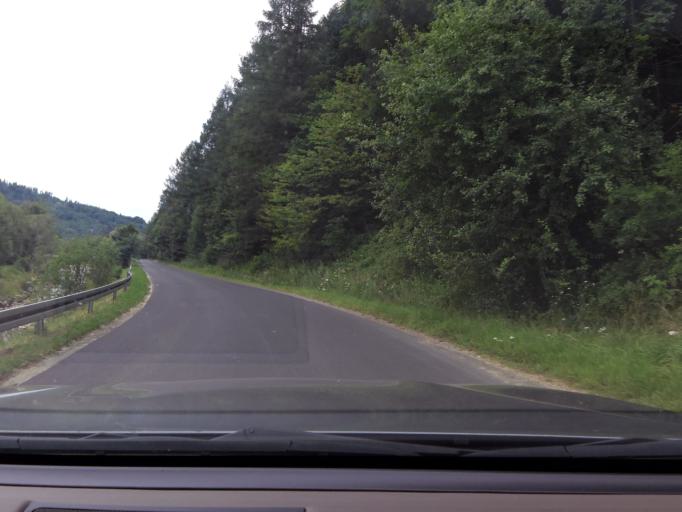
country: PL
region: Silesian Voivodeship
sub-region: Powiat zywiecki
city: Rajcza
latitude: 49.4929
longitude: 19.1198
